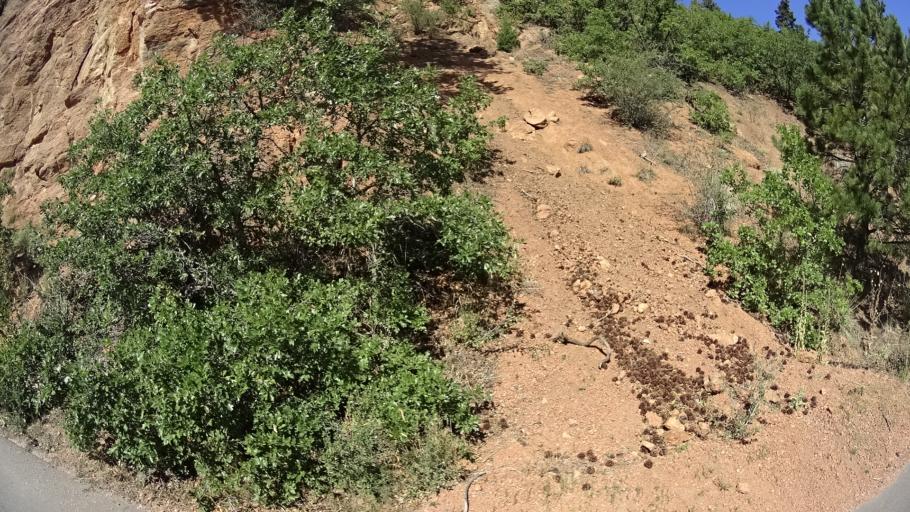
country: US
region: Colorado
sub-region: El Paso County
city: Manitou Springs
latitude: 38.8220
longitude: -104.8908
